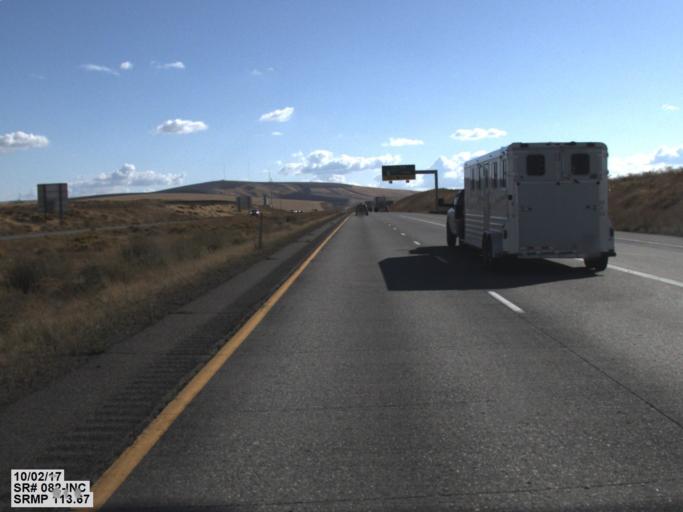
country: US
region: Washington
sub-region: Benton County
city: Kennewick
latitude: 46.1529
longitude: -119.2021
